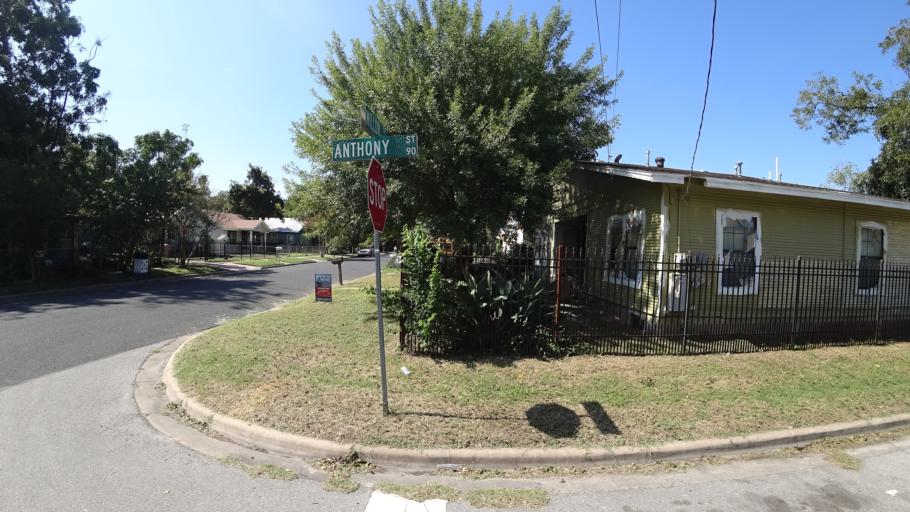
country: US
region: Texas
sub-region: Travis County
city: Austin
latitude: 30.2554
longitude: -97.7224
